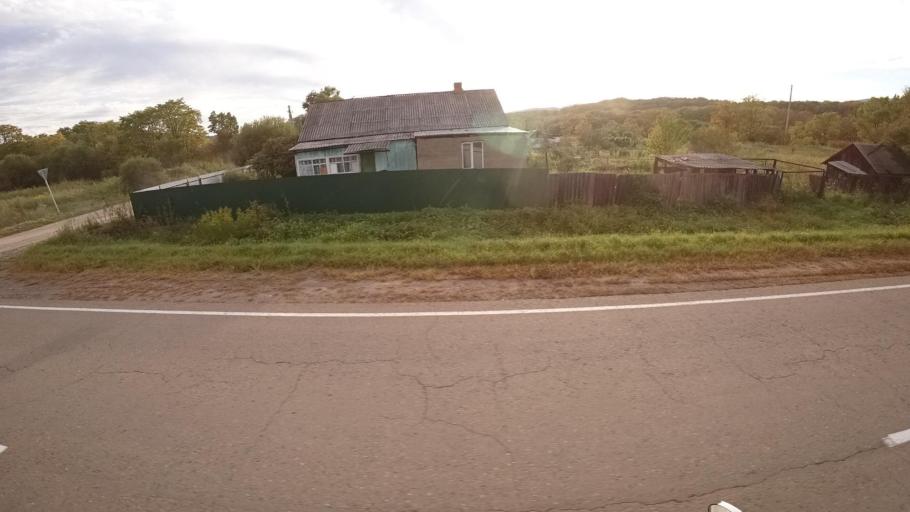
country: RU
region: Primorskiy
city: Yakovlevka
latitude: 44.4206
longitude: 133.4508
